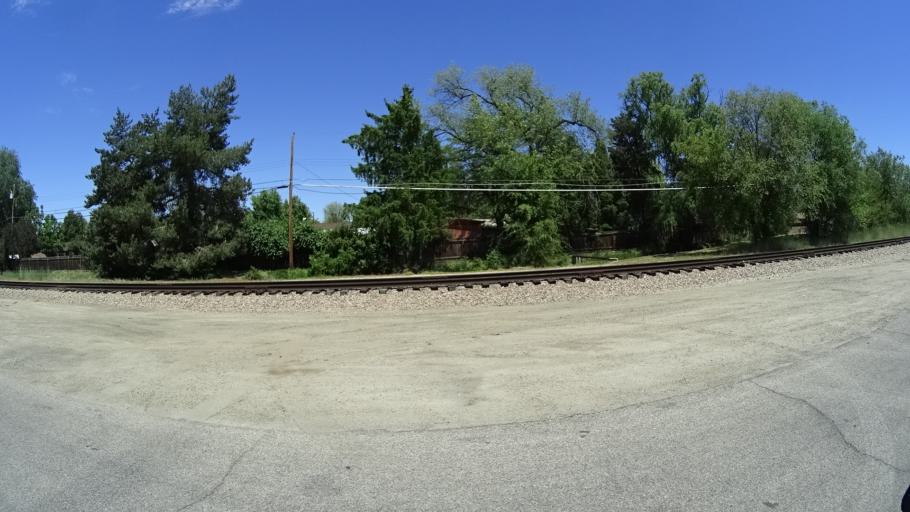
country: US
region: Idaho
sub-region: Ada County
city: Garden City
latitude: 43.6043
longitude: -116.2251
